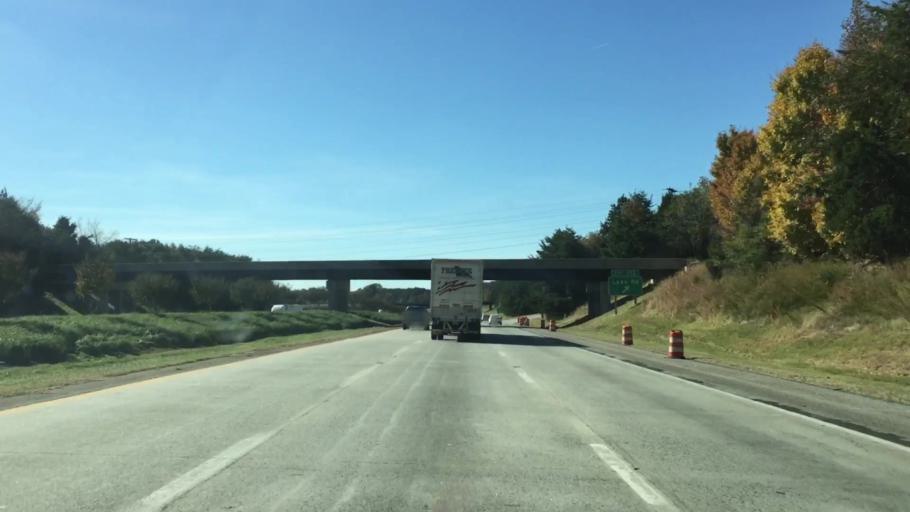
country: US
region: North Carolina
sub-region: Davidson County
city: Thomasville
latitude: 35.8549
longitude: -80.0954
